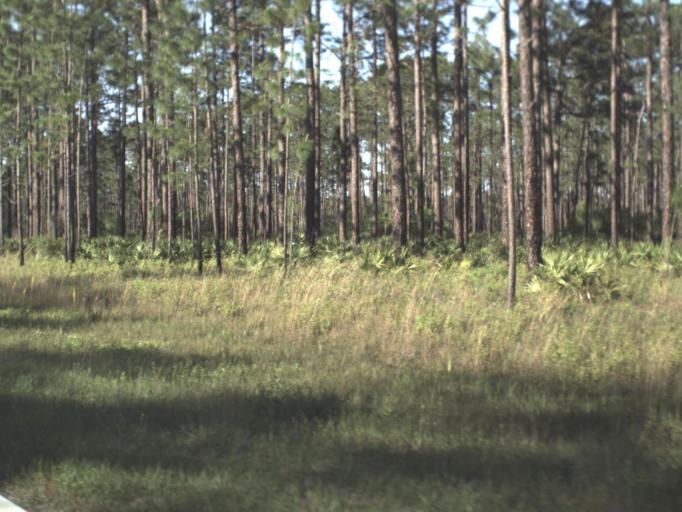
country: US
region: Florida
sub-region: Gulf County
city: Wewahitchka
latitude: 30.1205
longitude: -84.9884
